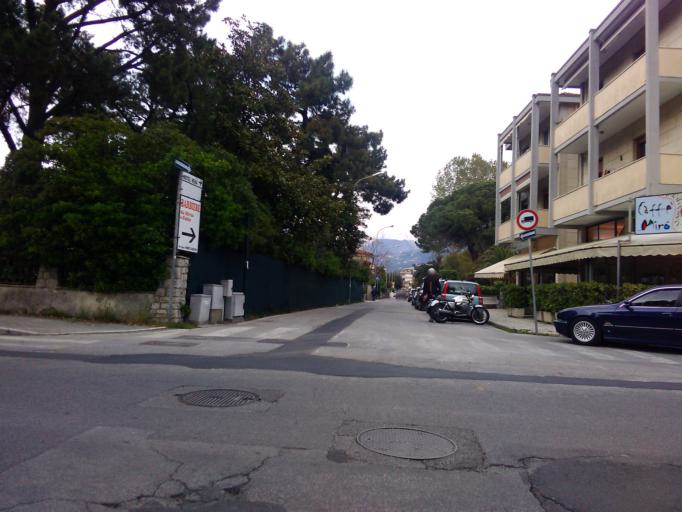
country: IT
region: Tuscany
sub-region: Provincia di Massa-Carrara
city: Massa
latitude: 44.0022
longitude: 10.1098
